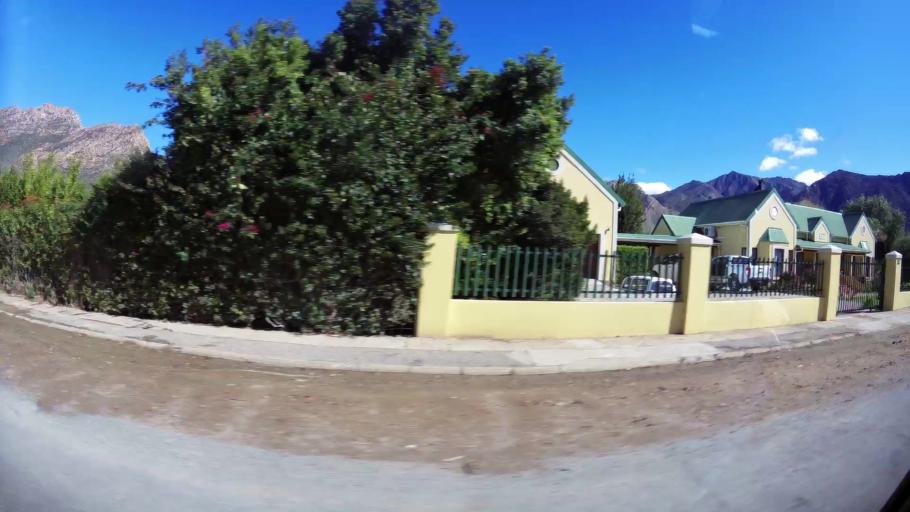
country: ZA
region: Western Cape
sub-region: Cape Winelands District Municipality
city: Ashton
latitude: -33.7908
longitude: 20.1200
